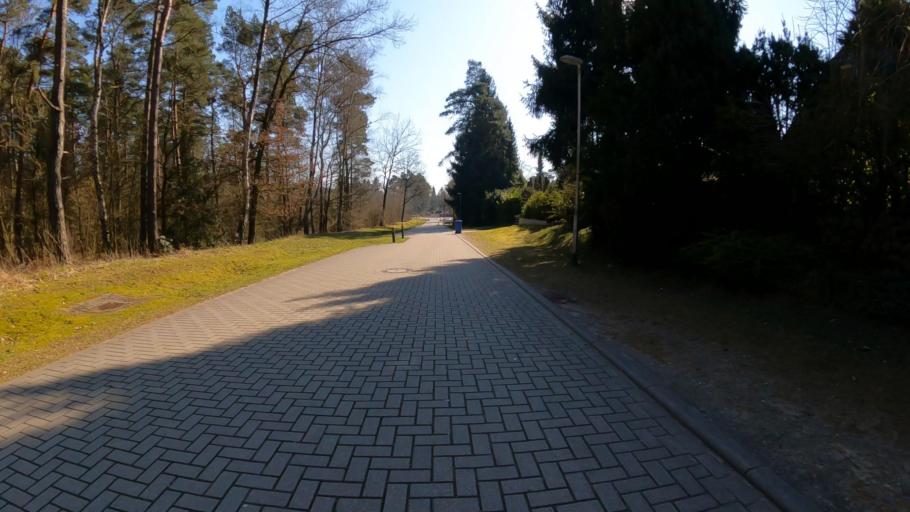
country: DE
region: Lower Saxony
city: Buchholz in der Nordheide
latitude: 53.3343
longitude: 9.9099
